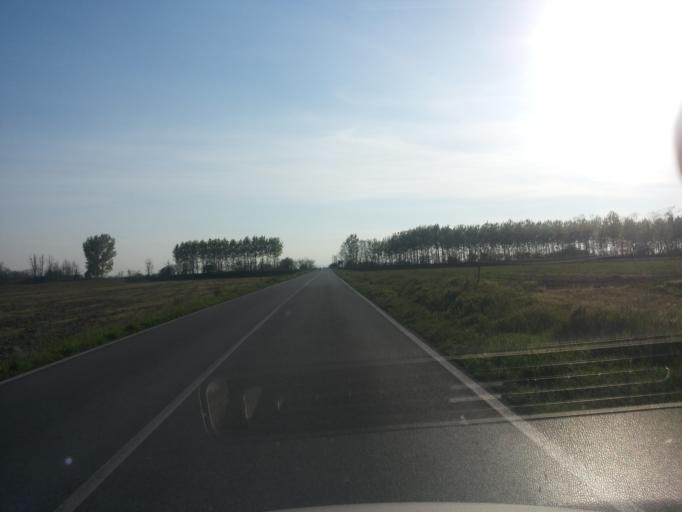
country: IT
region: Lombardy
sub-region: Provincia di Pavia
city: Cozzo
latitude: 45.2021
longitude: 8.6343
